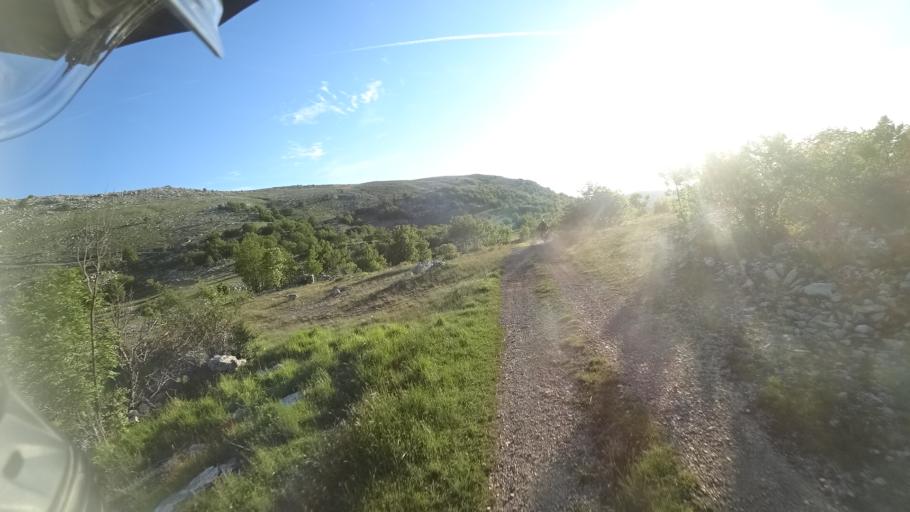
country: HR
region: Sibensko-Kniniska
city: Drnis
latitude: 43.8705
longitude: 16.3711
